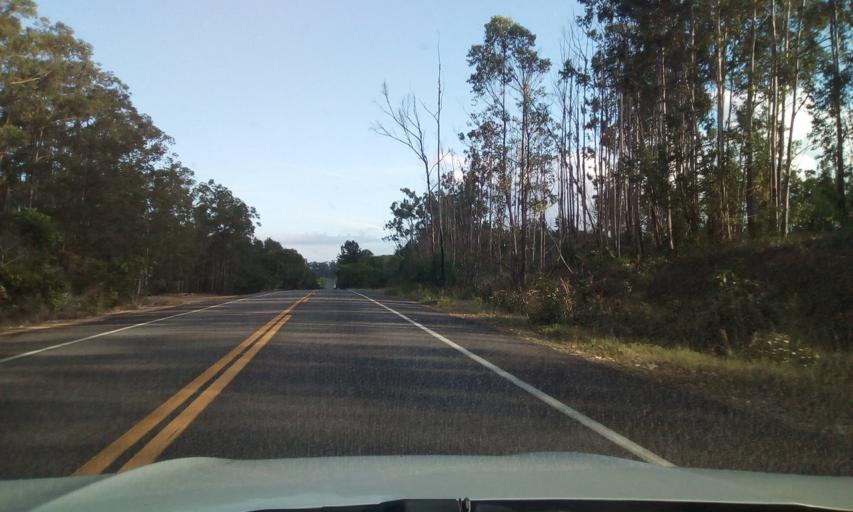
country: BR
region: Bahia
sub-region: Entre Rios
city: Entre Rios
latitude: -12.3184
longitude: -37.9044
